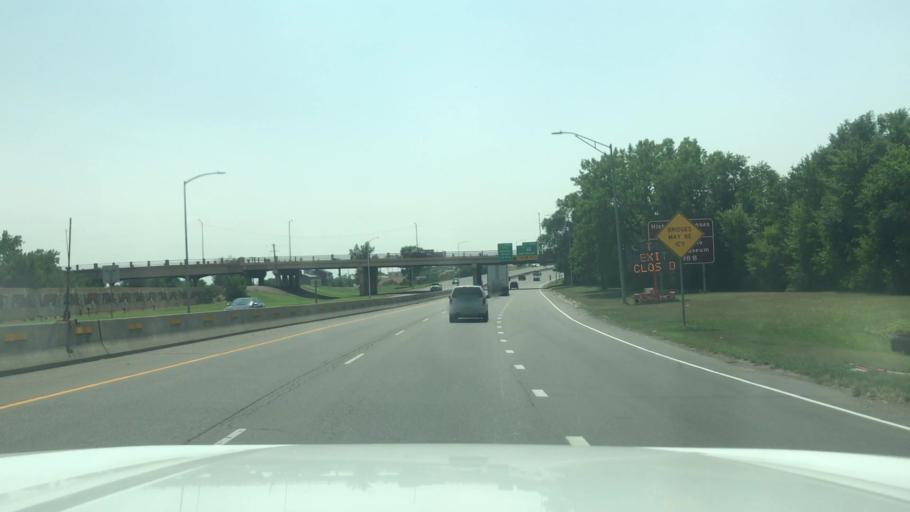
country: US
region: Colorado
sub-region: Pueblo County
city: Pueblo
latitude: 38.2760
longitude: -104.6041
